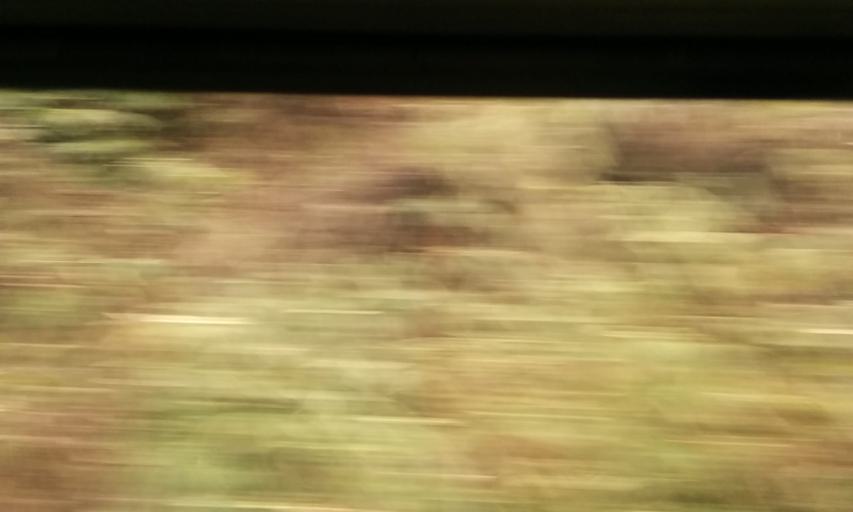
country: JP
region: Gifu
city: Nakatsugawa
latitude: 35.6761
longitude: 137.6404
